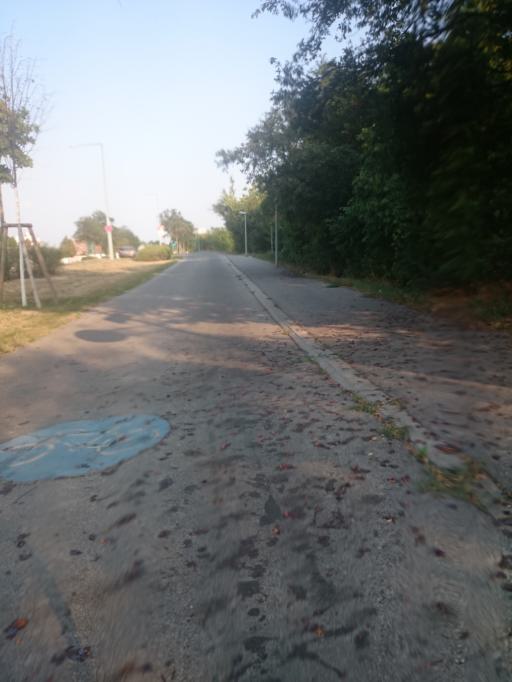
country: AT
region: Lower Austria
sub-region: Politischer Bezirk Wien-Umgebung
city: Gerasdorf bei Wien
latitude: 48.2556
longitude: 16.4232
